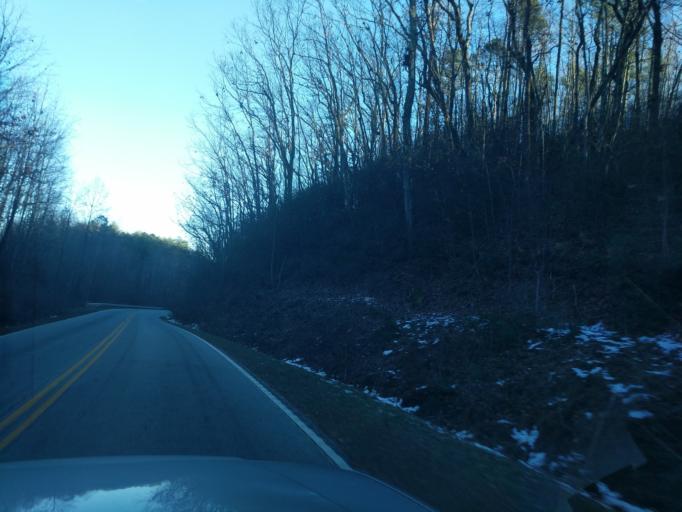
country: US
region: South Carolina
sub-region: Oconee County
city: Westminster
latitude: 34.7375
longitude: -83.2362
